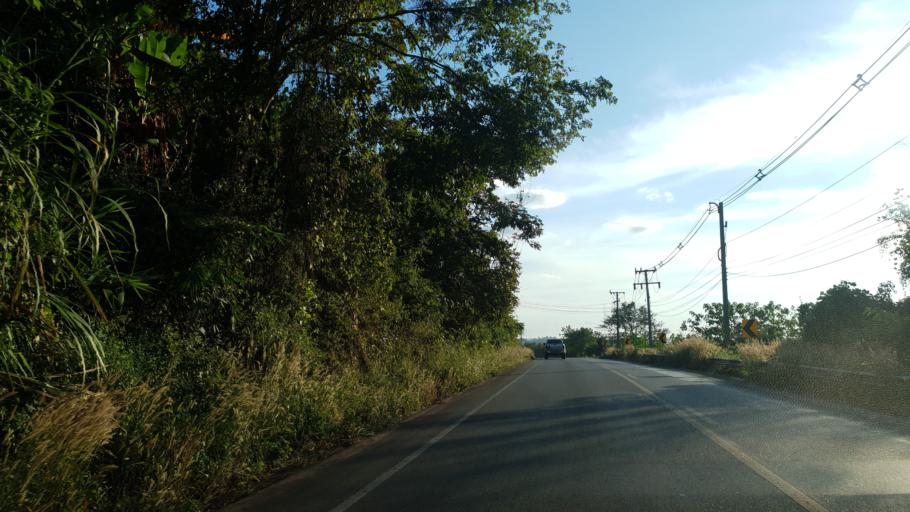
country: TH
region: Loei
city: Dan Sai
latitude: 17.2130
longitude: 101.0195
